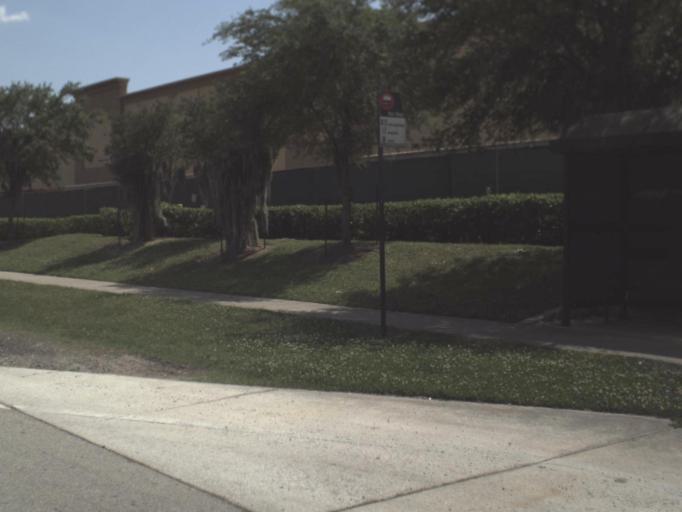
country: US
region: Florida
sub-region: Duval County
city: Jacksonville
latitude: 30.2800
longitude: -81.6283
